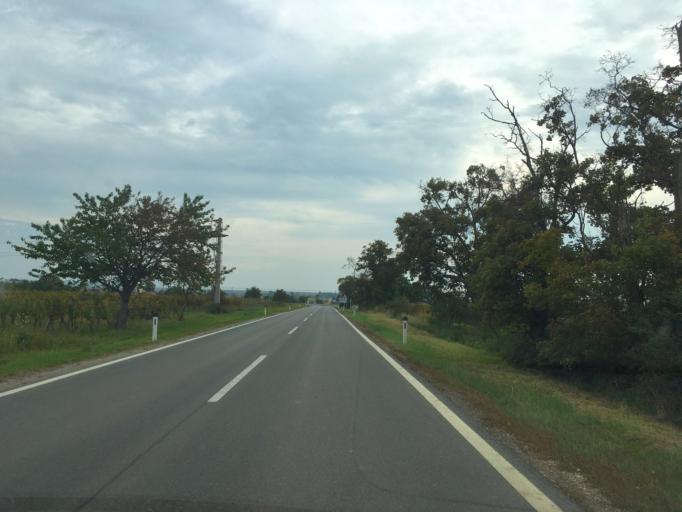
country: AT
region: Burgenland
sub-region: Politischer Bezirk Neusiedl am See
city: Winden am See
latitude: 47.9519
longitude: 16.7424
